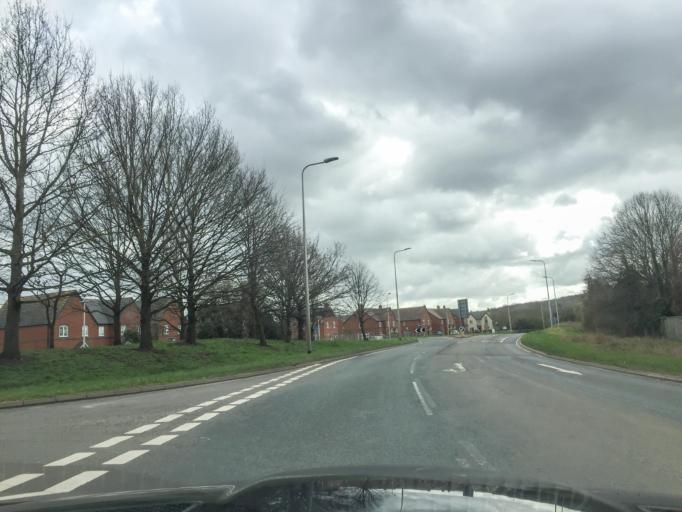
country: GB
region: England
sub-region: Warwickshire
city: Wellesbourne Mountford
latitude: 52.1899
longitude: -1.5980
